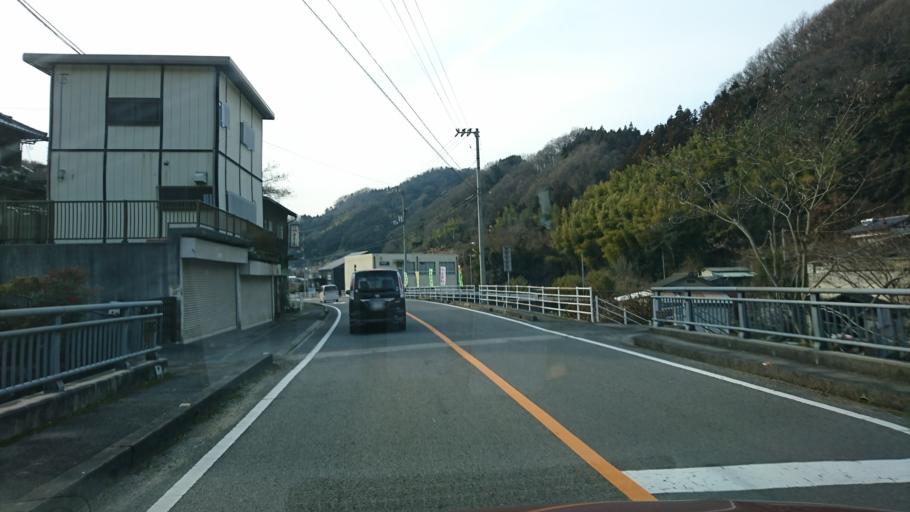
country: JP
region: Ehime
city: Hojo
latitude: 33.9000
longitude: 132.8692
